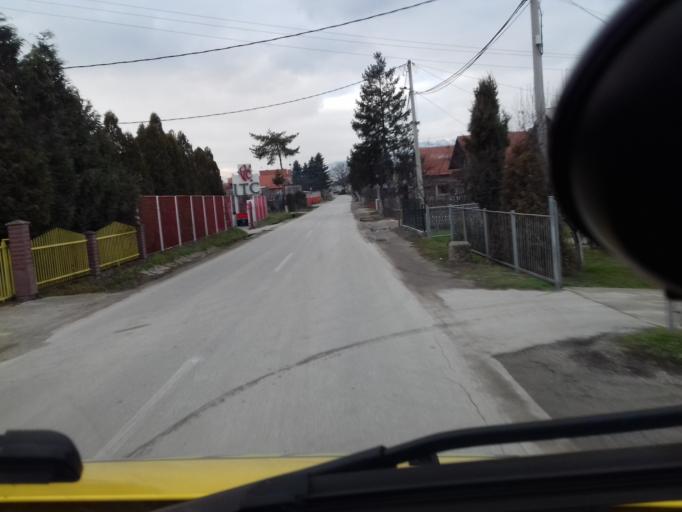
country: BA
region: Federation of Bosnia and Herzegovina
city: Zenica
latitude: 44.1827
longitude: 17.9584
